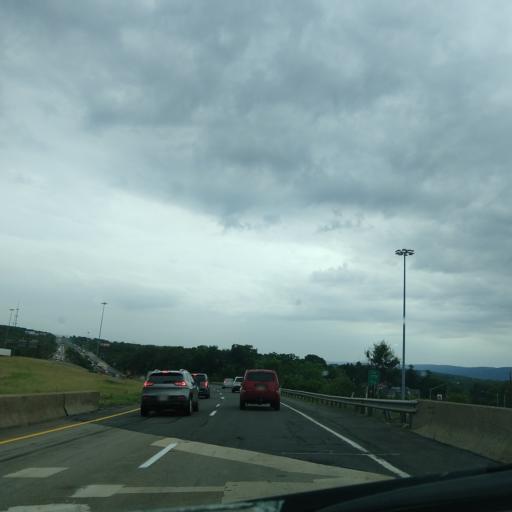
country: US
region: Pennsylvania
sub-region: Lackawanna County
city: Moosic
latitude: 41.3561
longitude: -75.7212
